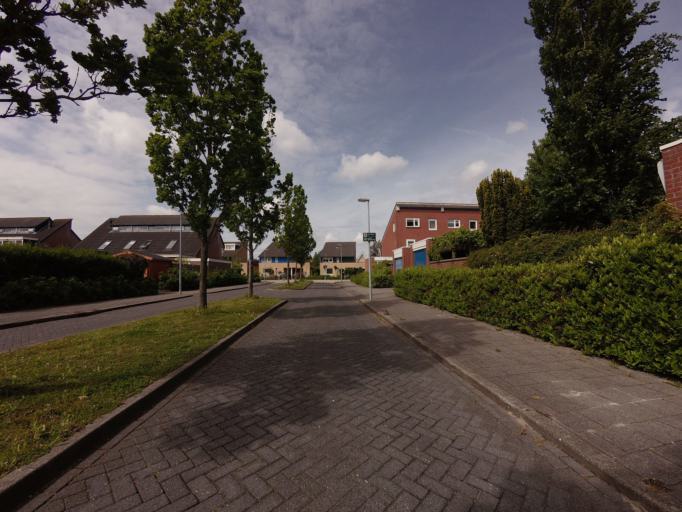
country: NL
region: North Holland
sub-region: Gemeente Hoorn
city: Hoorn
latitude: 52.6785
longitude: 5.0202
